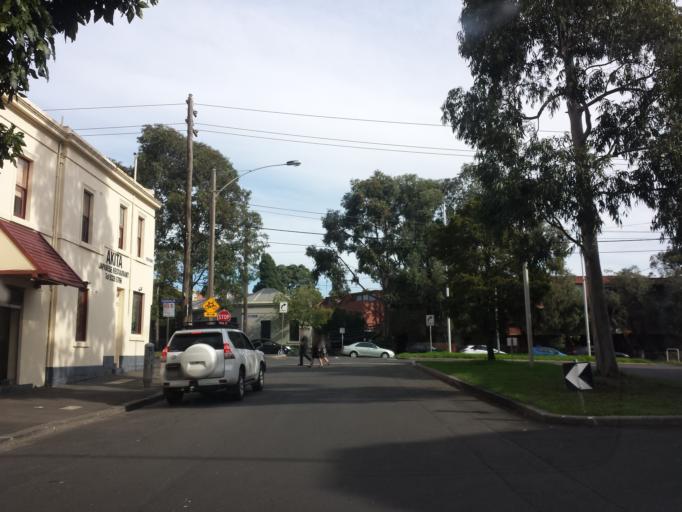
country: AU
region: Victoria
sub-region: Melbourne
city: North Melbourne
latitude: -37.8019
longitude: 144.9545
